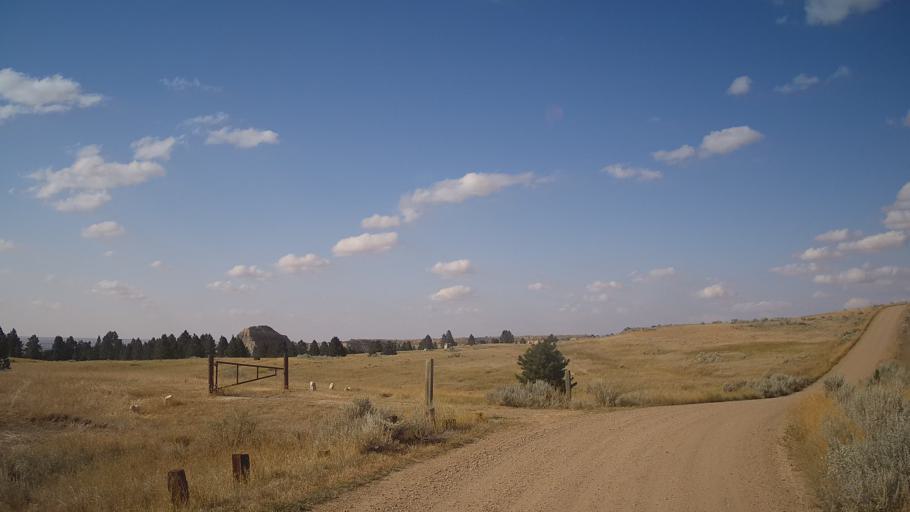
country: US
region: Montana
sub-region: Dawson County
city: Glendive
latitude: 47.0594
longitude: -104.6715
